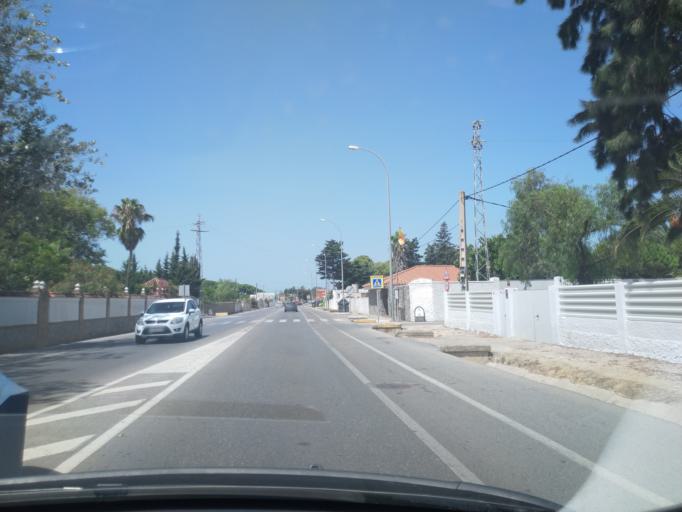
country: ES
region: Andalusia
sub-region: Provincia de Cadiz
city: Chiclana de la Frontera
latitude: 36.3943
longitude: -6.1548
